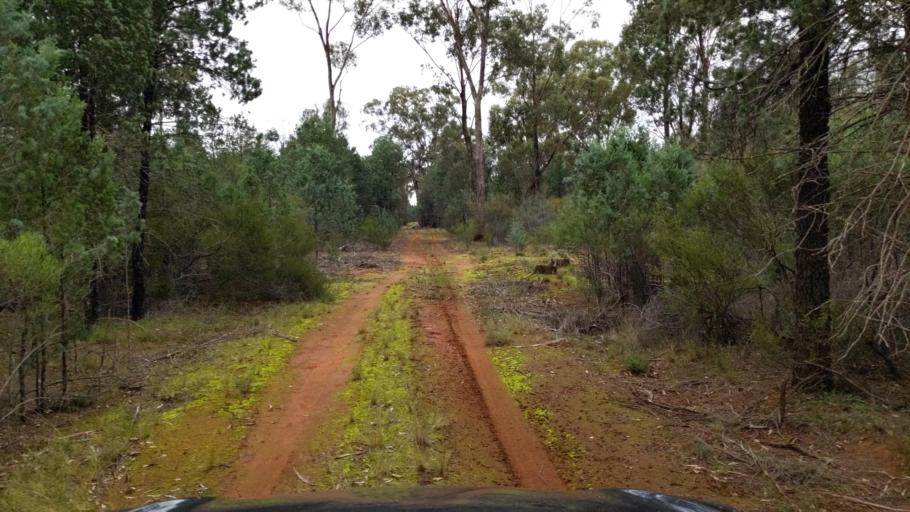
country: AU
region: New South Wales
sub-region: Coolamon
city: Coolamon
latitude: -34.8509
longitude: 146.9318
